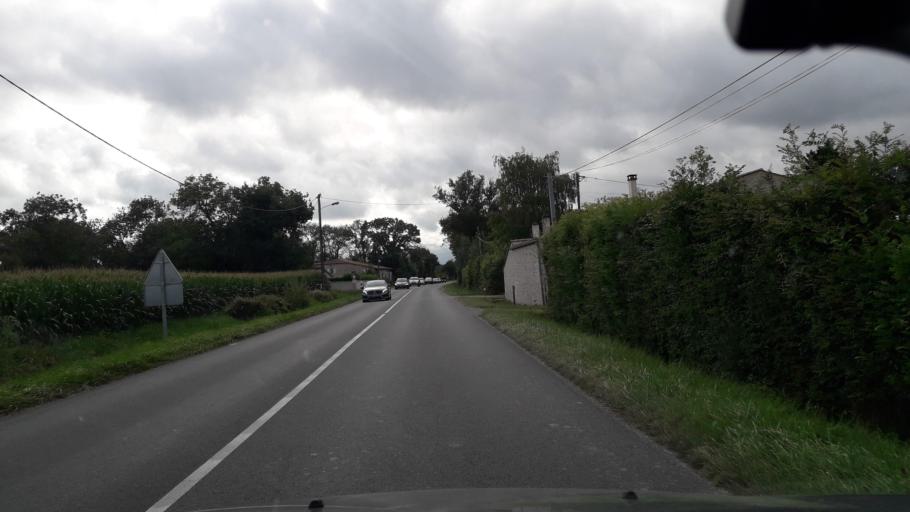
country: FR
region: Poitou-Charentes
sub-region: Departement de la Charente-Maritime
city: Medis
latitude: 45.6750
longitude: -0.9678
